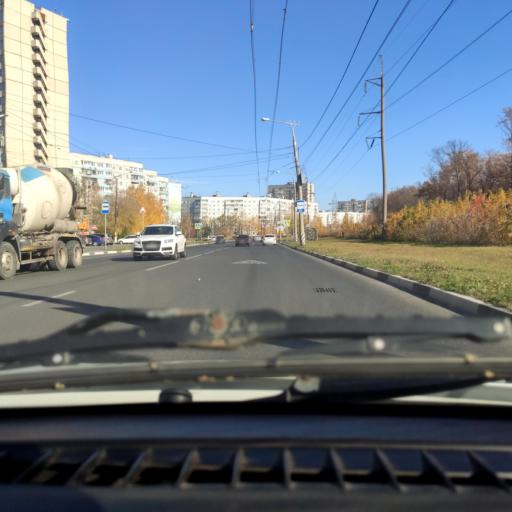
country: RU
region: Samara
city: Tol'yatti
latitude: 53.5033
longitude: 49.4288
